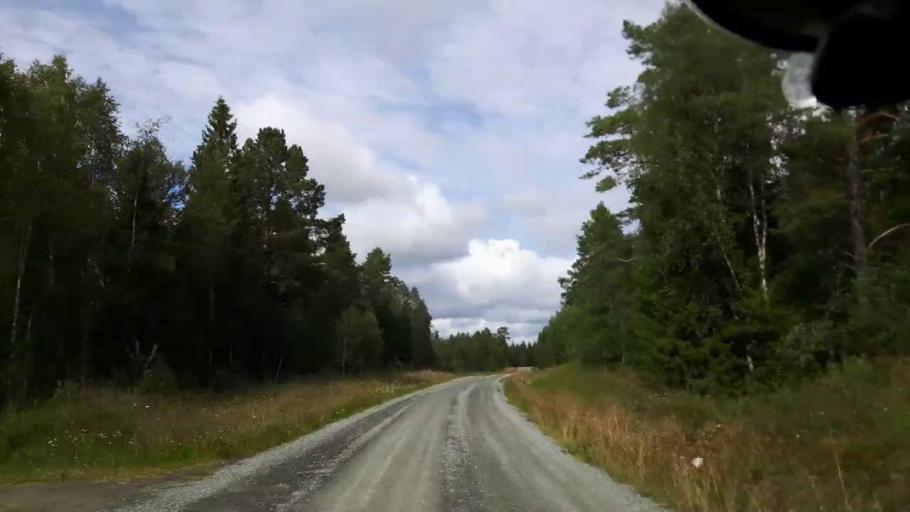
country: SE
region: Jaemtland
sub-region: Krokoms Kommun
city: Valla
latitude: 63.5444
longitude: 13.9172
